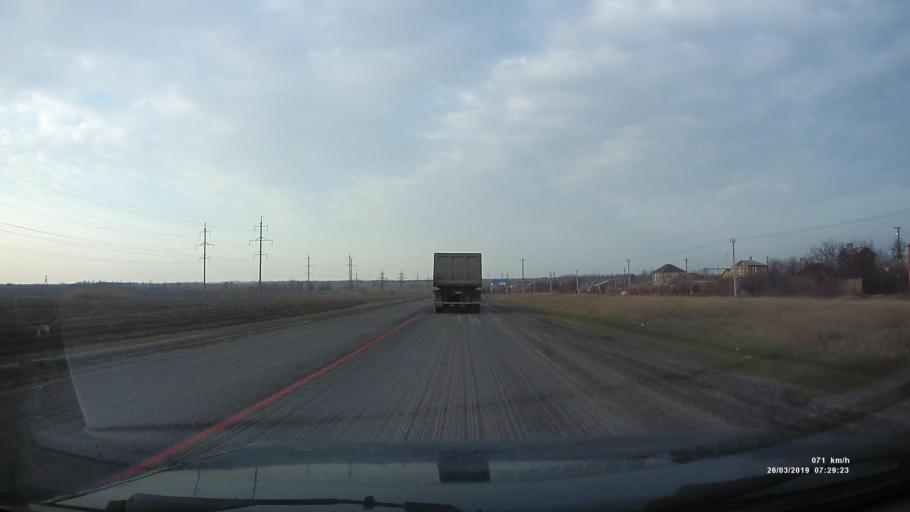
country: RU
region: Rostov
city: Novobessergenovka
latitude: 47.2456
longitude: 38.8169
